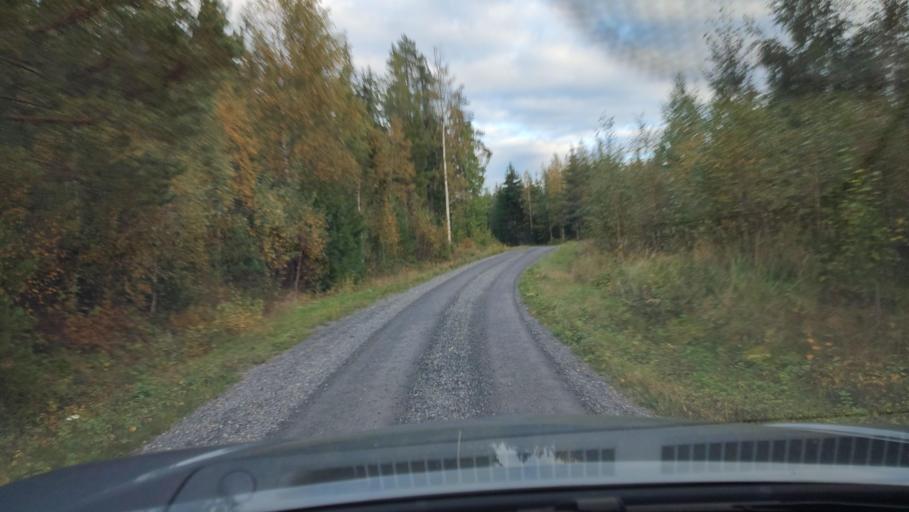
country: FI
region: Ostrobothnia
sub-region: Sydosterbotten
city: Kristinestad
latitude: 62.2324
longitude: 21.4113
